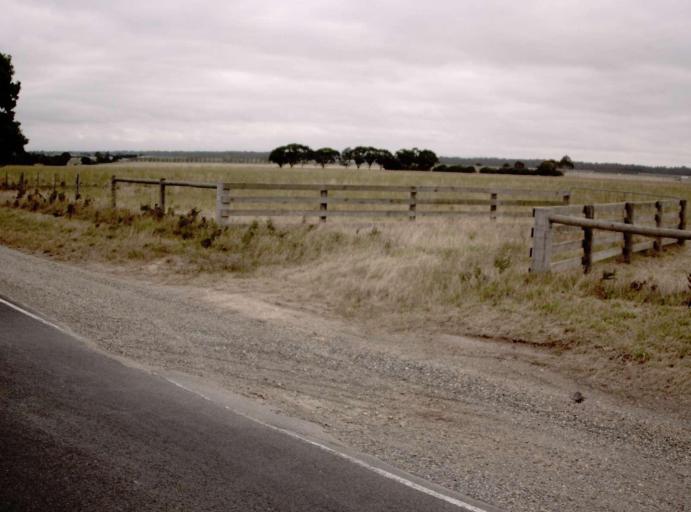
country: AU
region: Victoria
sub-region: Wellington
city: Sale
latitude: -38.0955
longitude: 146.9871
